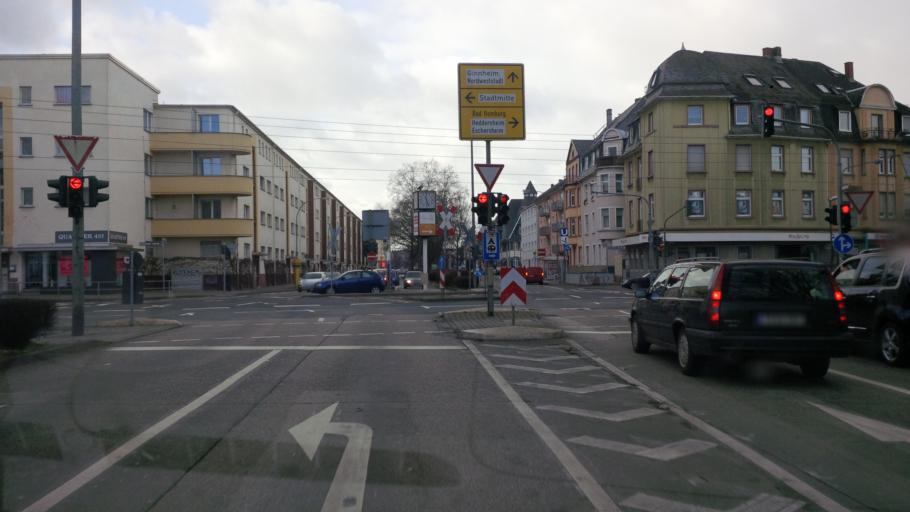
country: DE
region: Hesse
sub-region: Regierungsbezirk Darmstadt
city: Frankfurt am Main
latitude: 50.1481
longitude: 8.6667
